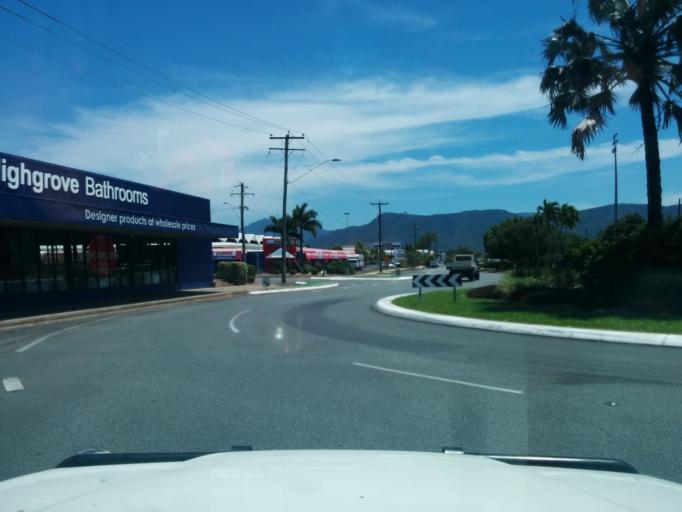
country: AU
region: Queensland
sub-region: Cairns
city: Cairns
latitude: -16.9302
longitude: 145.7690
